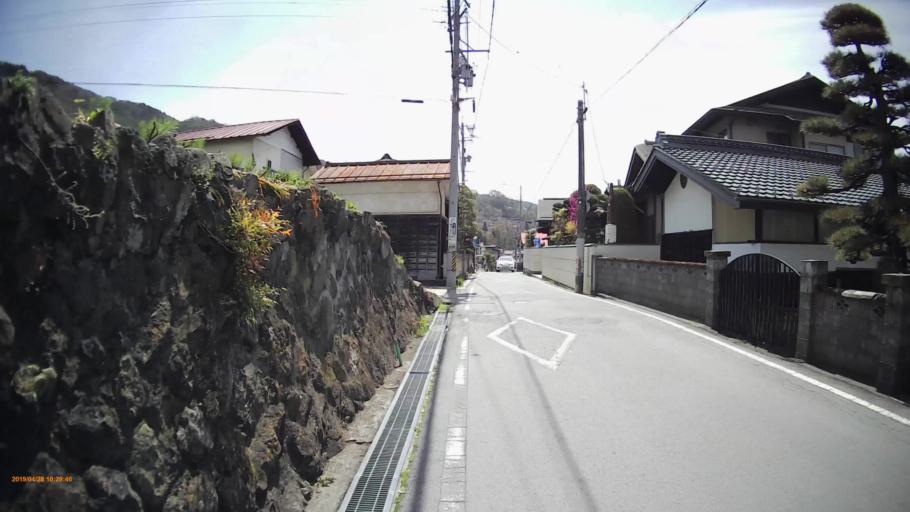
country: JP
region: Nagano
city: Suwa
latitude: 36.0580
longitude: 138.1146
